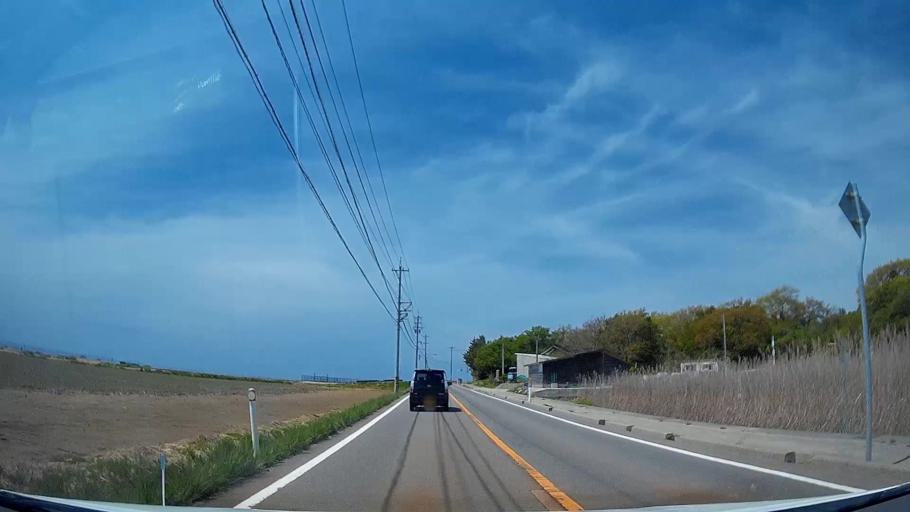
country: JP
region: Ishikawa
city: Hakui
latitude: 36.9284
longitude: 136.7578
